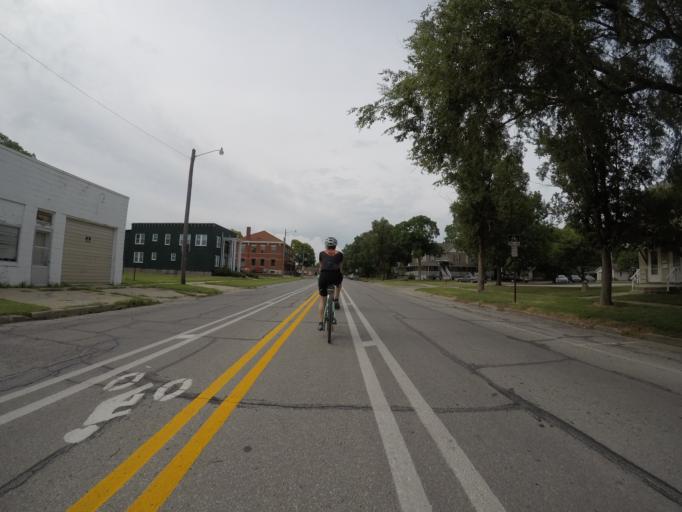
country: US
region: Kansas
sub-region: Franklin County
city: Ottawa
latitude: 38.6140
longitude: -95.2700
